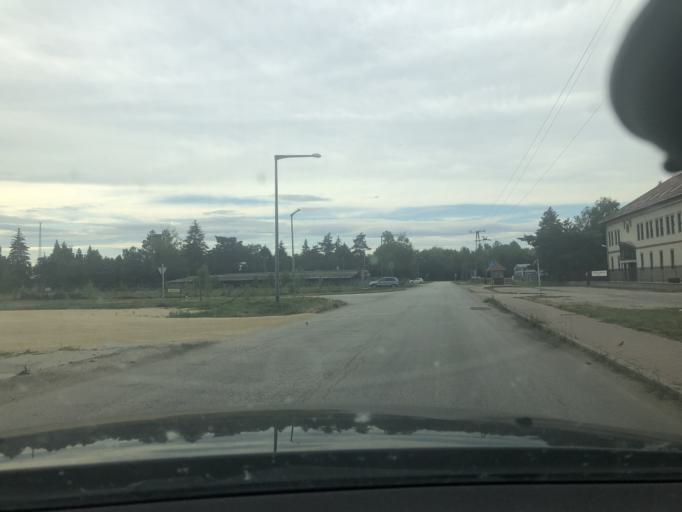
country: HU
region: Gyor-Moson-Sopron
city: Kapuvar
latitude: 47.5892
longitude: 17.0445
